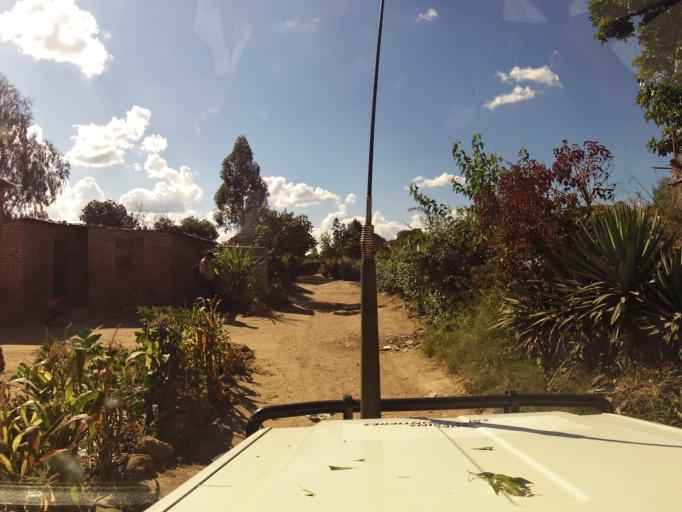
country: ZW
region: Harare
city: Epworth
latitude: -17.8780
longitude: 31.1361
